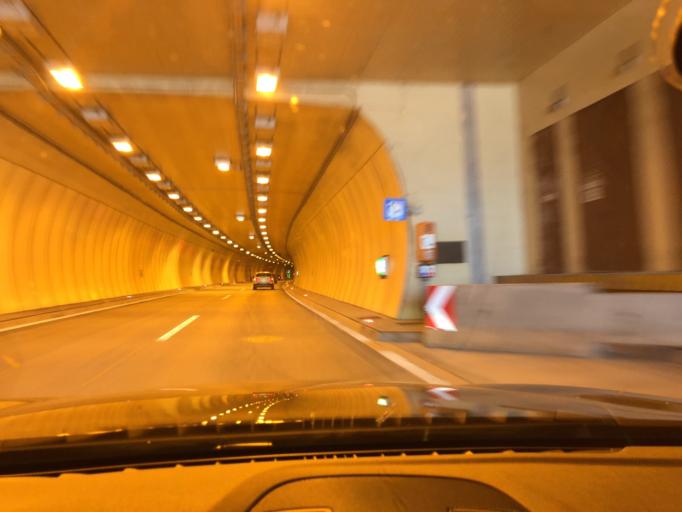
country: AT
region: Tyrol
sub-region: Politischer Bezirk Imst
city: Roppen
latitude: 47.2265
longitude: 10.8165
